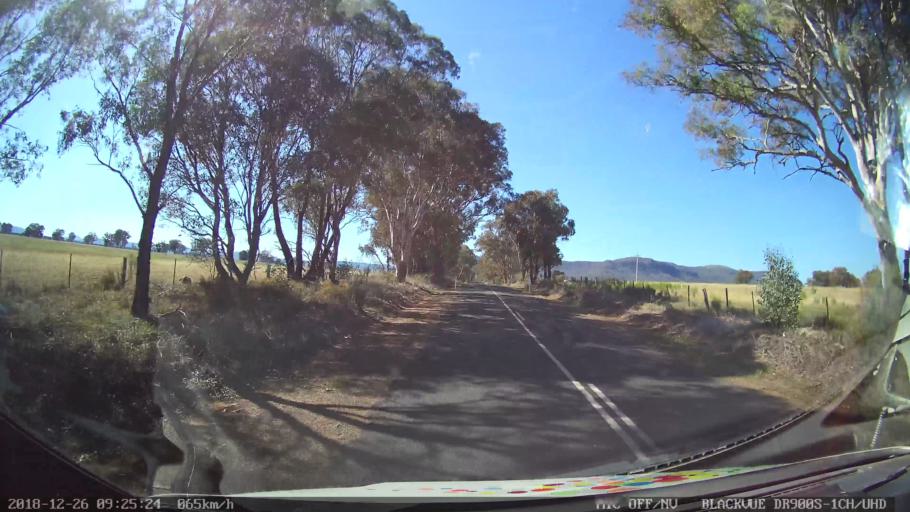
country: AU
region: New South Wales
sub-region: Mid-Western Regional
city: Kandos
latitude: -32.8195
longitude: 150.0035
